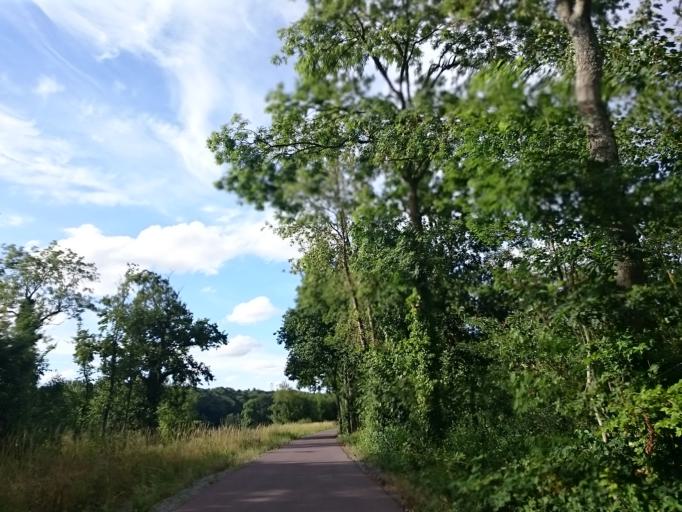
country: FR
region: Lower Normandy
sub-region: Departement du Calvados
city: Saint-Andre-sur-Orne
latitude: 49.1276
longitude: -0.4023
